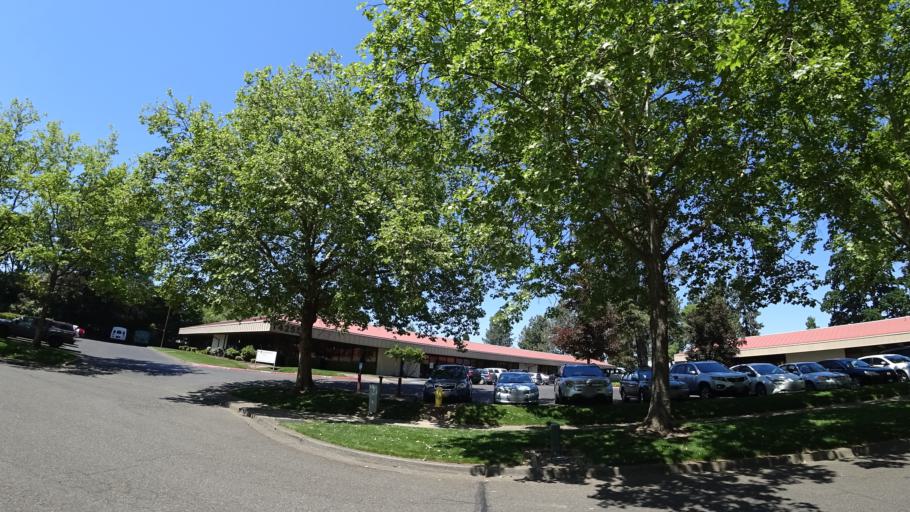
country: US
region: Oregon
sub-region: Washington County
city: Beaverton
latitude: 45.4927
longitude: -122.8230
